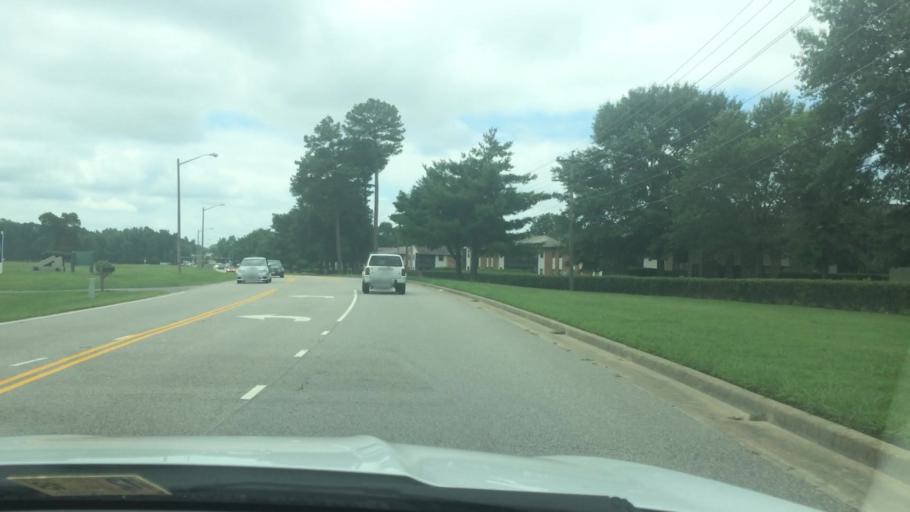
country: US
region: Virginia
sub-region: York County
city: Yorktown
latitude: 37.2119
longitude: -76.5721
